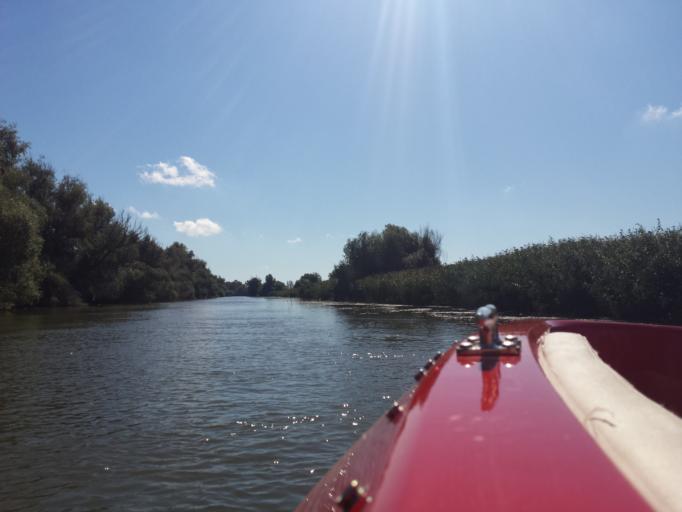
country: RO
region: Tulcea
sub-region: Comuna Mahmudia
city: Mahmudia
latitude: 45.2166
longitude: 29.1738
